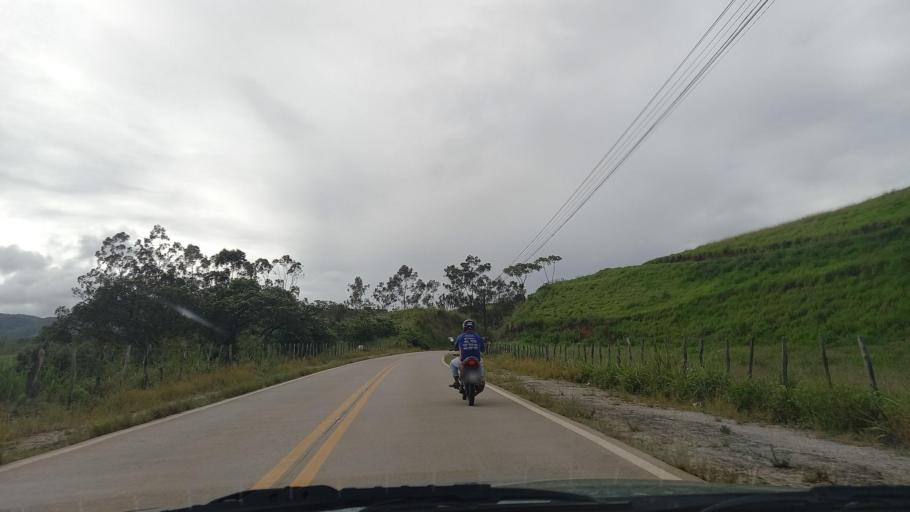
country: BR
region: Pernambuco
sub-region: Maraial
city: Maraial
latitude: -8.7405
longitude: -35.7995
